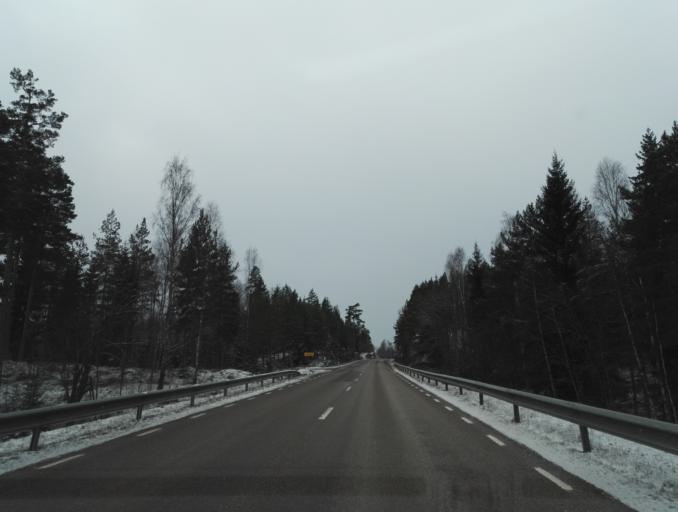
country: SE
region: Kalmar
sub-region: Hultsfreds Kommun
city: Virserum
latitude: 57.2649
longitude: 15.5621
